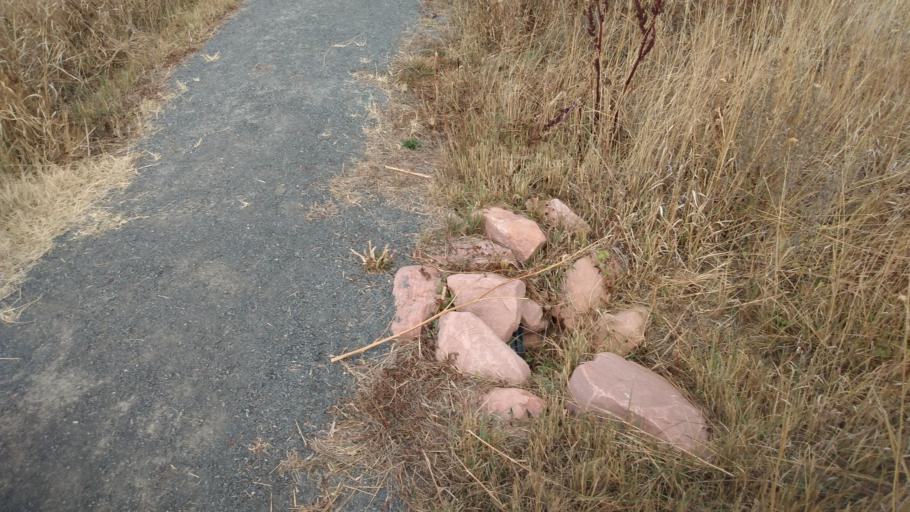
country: US
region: Colorado
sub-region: Boulder County
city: Gunbarrel
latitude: 40.0111
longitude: -105.2029
